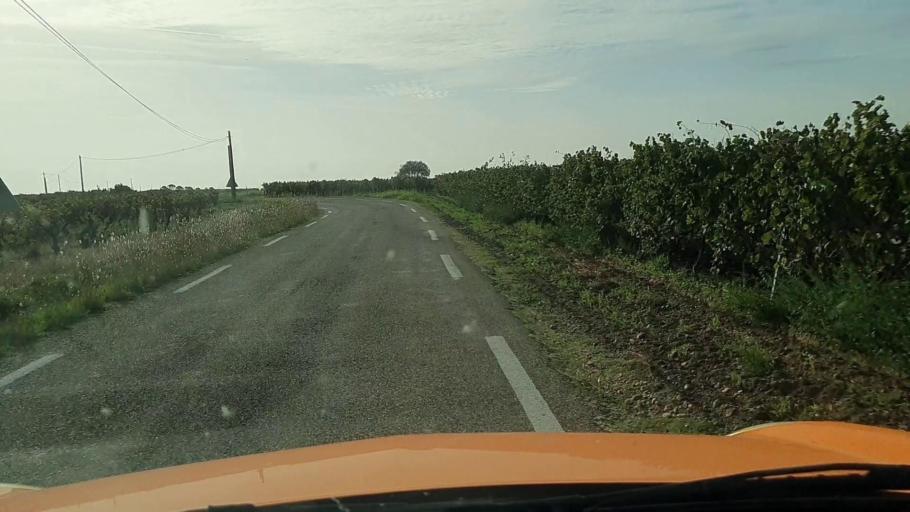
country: FR
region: Languedoc-Roussillon
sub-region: Departement du Gard
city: Beauvoisin
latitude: 43.7077
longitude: 4.3401
